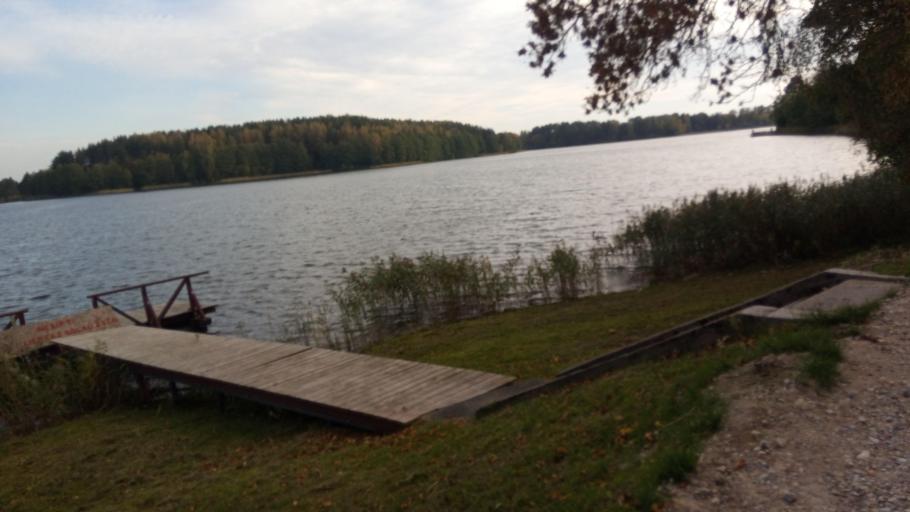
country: LT
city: Trakai
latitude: 54.6383
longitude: 24.9422
